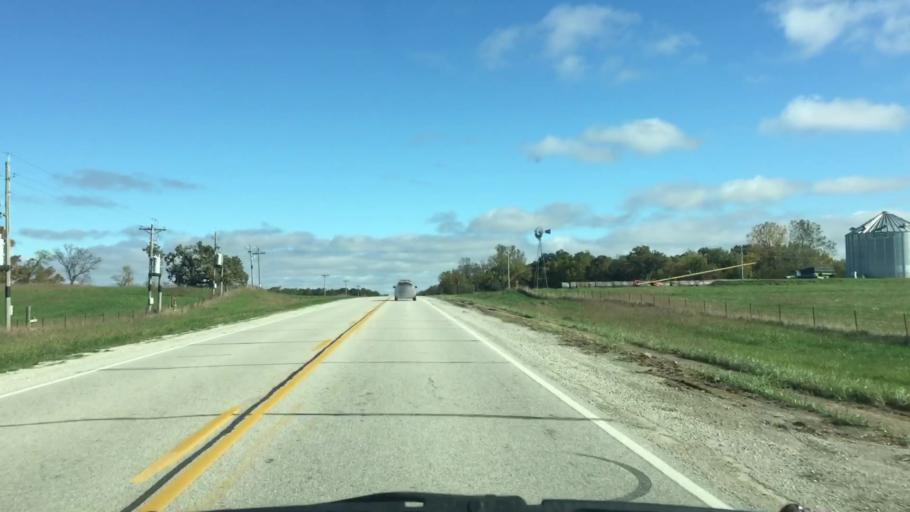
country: US
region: Iowa
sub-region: Decatur County
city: Leon
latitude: 40.6474
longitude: -93.8035
